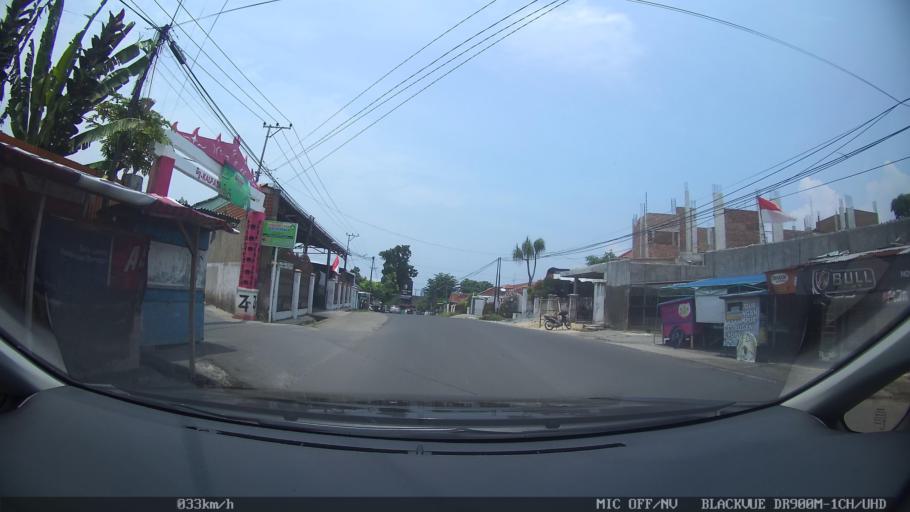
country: ID
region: Lampung
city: Bandarlampung
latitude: -5.4387
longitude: 105.2745
